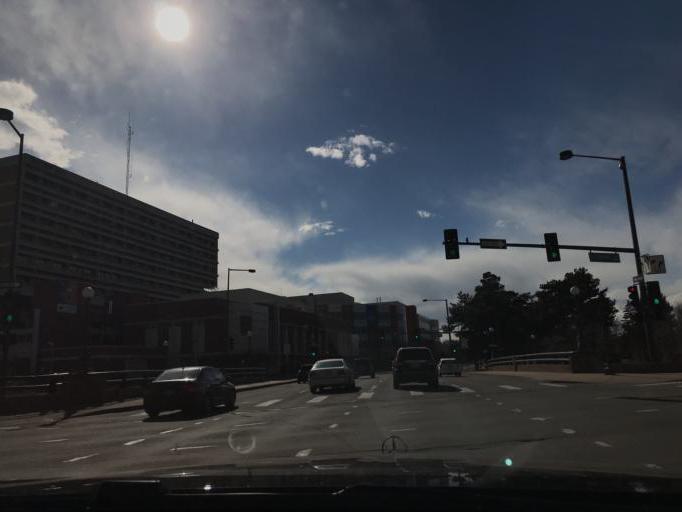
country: US
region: Colorado
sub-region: Denver County
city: Denver
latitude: 39.7291
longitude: -104.9898
